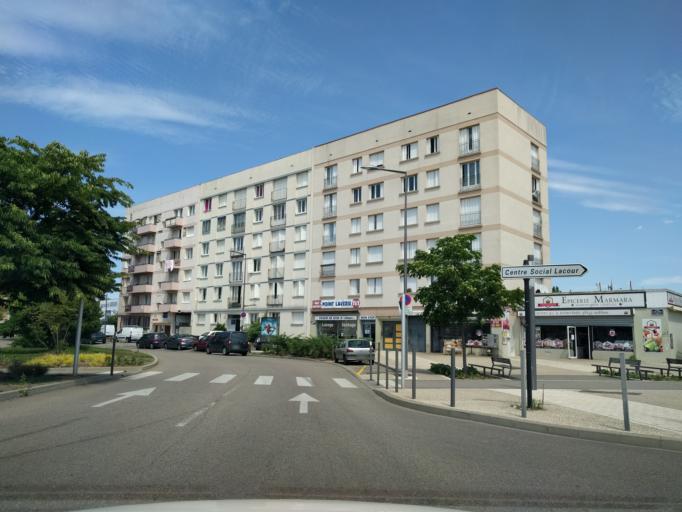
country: FR
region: Lorraine
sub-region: Departement de la Moselle
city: Metz
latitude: 49.1338
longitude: 6.1702
